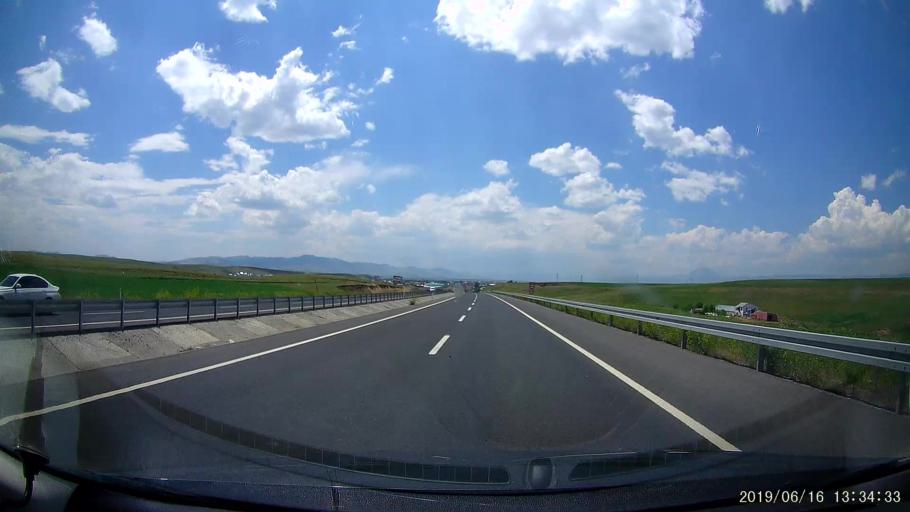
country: TR
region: Agri
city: Agri
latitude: 39.7130
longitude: 43.1232
